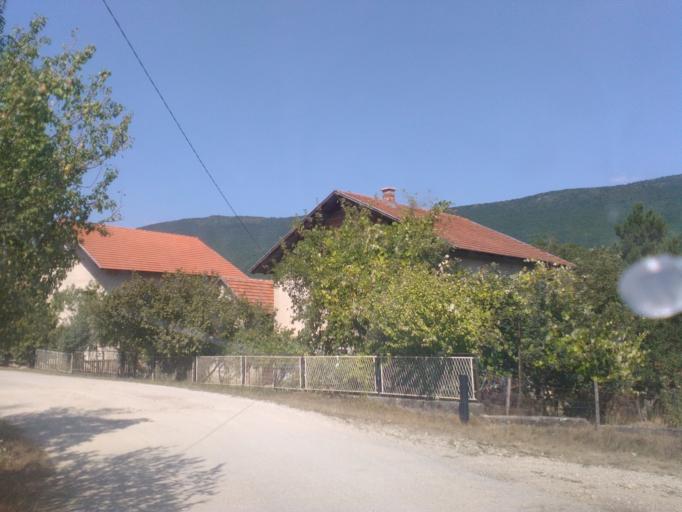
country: BA
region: Federation of Bosnia and Herzegovina
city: Orasac
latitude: 44.6232
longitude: 16.0655
